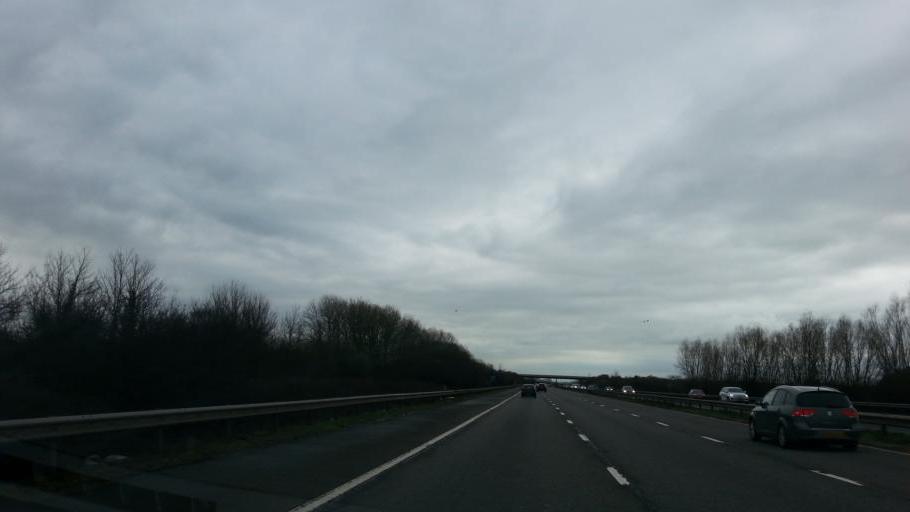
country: GB
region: England
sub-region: Somerset
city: Puriton
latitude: 51.1474
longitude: -2.9773
